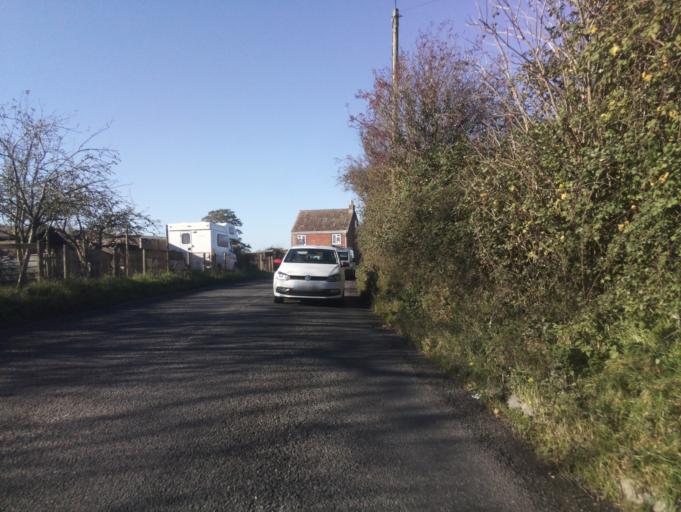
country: GB
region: England
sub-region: Somerset
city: Ilchester
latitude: 50.9657
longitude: -2.6824
